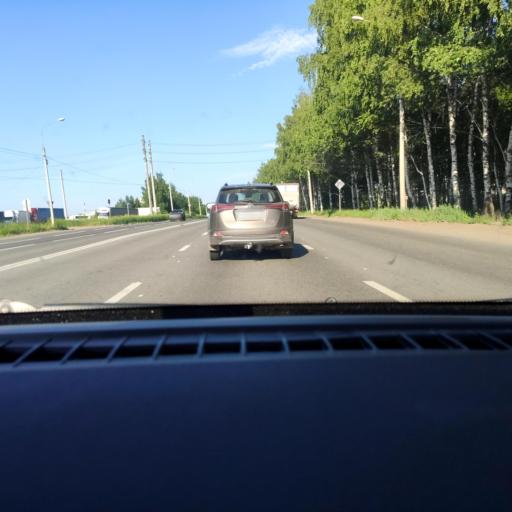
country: RU
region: Udmurtiya
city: Khokhryaki
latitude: 56.9077
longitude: 53.3547
